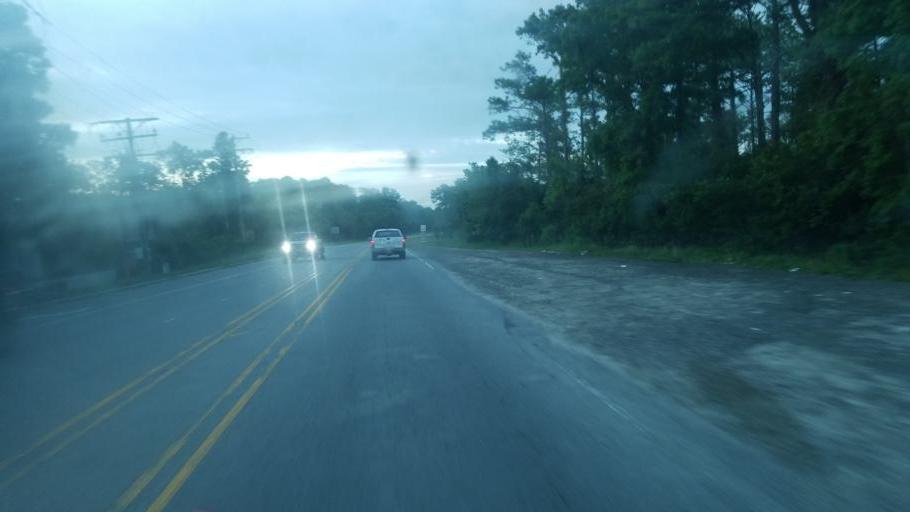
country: US
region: North Carolina
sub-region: Dare County
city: Manteo
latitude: 35.8891
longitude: -75.6606
